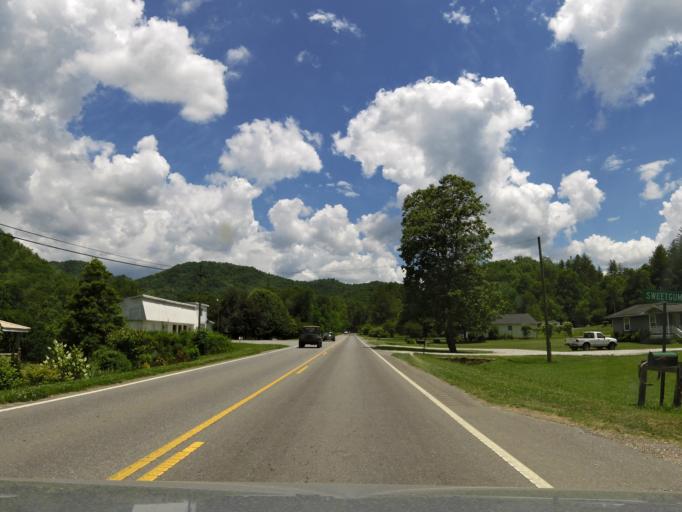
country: US
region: North Carolina
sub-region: Graham County
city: Robbinsville
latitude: 35.2892
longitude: -83.7714
